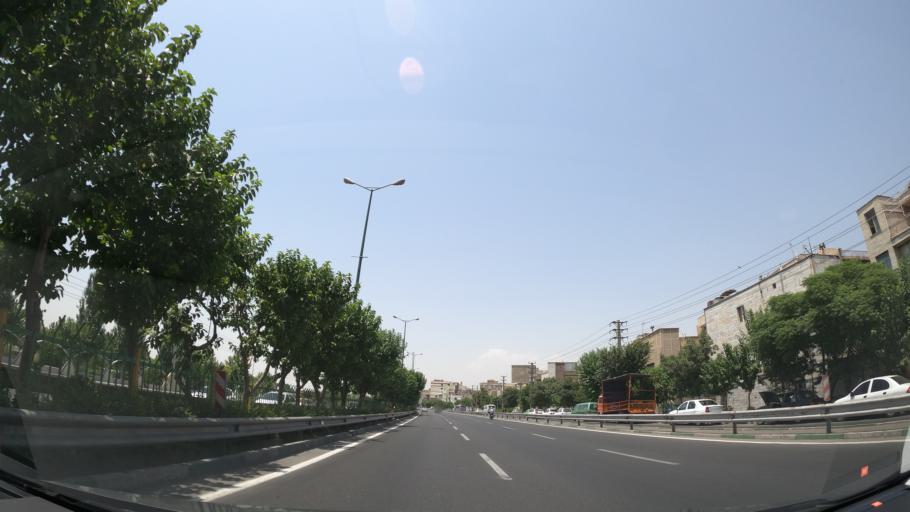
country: IR
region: Tehran
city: Tehran
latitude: 35.6497
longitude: 51.3891
